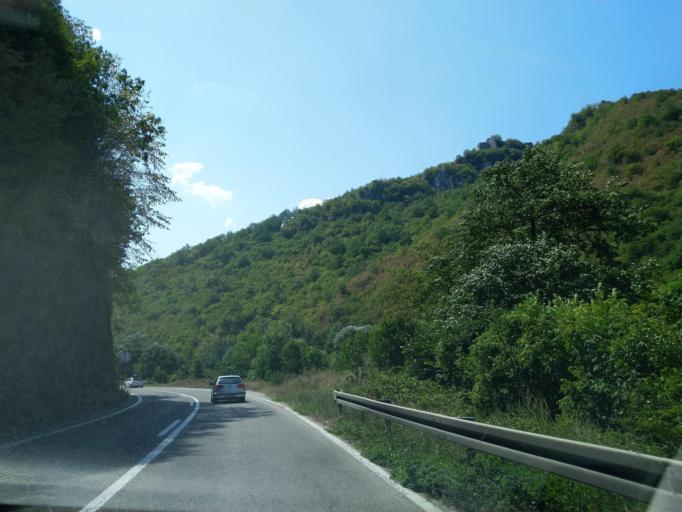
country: RS
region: Central Serbia
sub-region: Zlatiborski Okrug
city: Prijepolje
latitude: 43.4560
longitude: 19.6434
